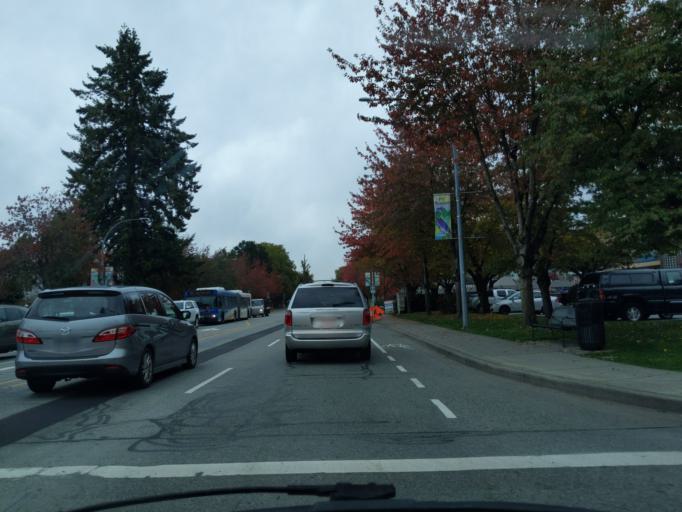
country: CA
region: British Columbia
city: Pitt Meadows
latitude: 49.2245
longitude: -122.6897
